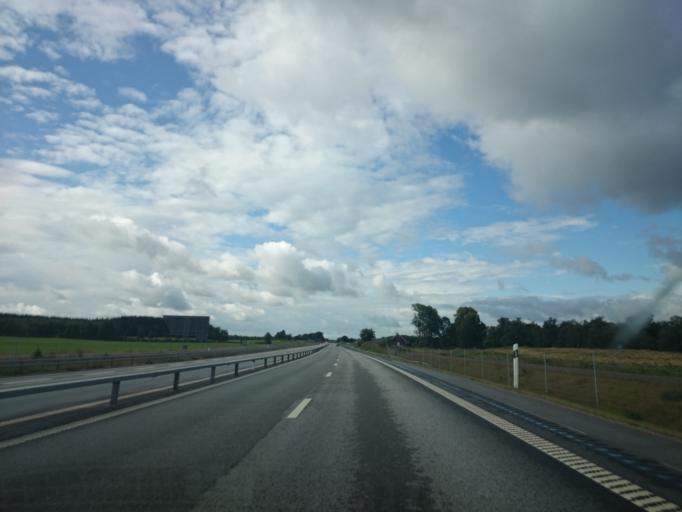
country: SE
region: Skane
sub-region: Horby Kommun
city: Hoerby
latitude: 55.8972
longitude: 13.7239
